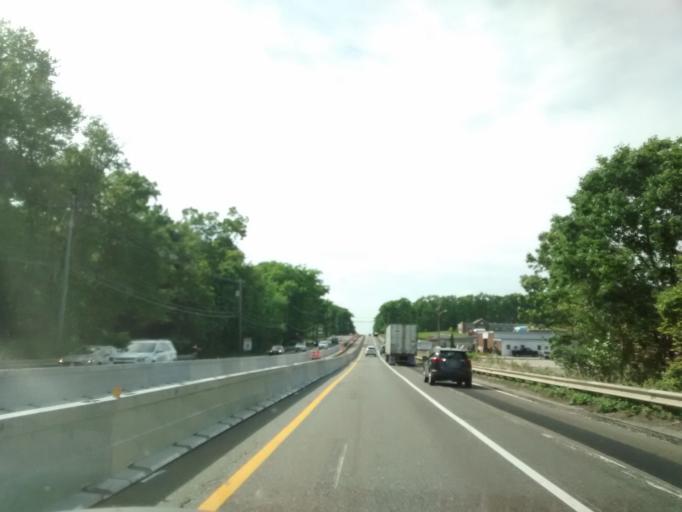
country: US
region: Massachusetts
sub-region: Worcester County
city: Sutton
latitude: 42.1676
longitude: -71.7472
